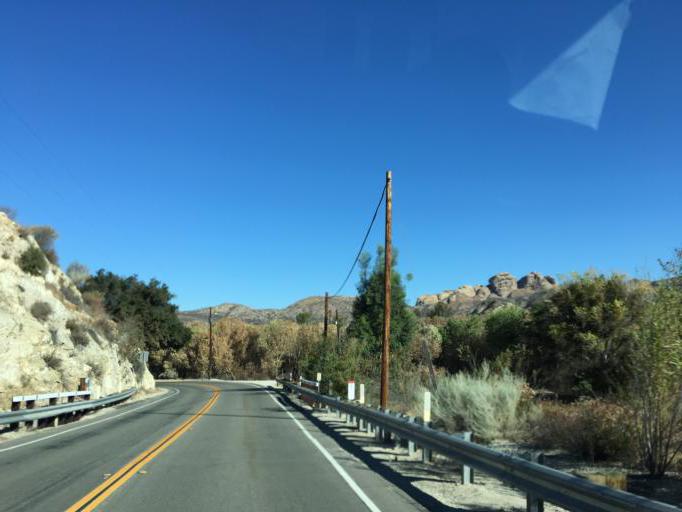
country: US
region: California
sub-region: Los Angeles County
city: Agua Dulce
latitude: 34.4382
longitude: -118.2785
